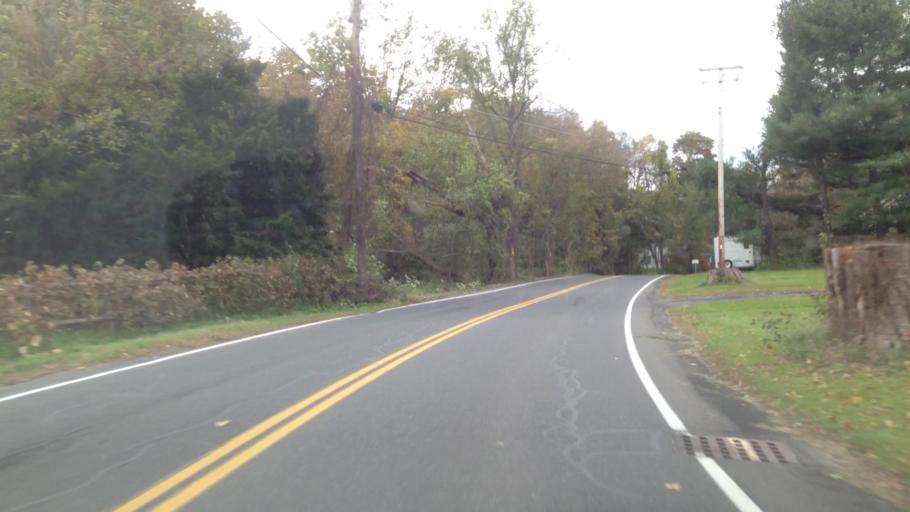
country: US
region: New York
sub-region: Ulster County
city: Tillson
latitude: 41.8268
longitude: -74.0754
